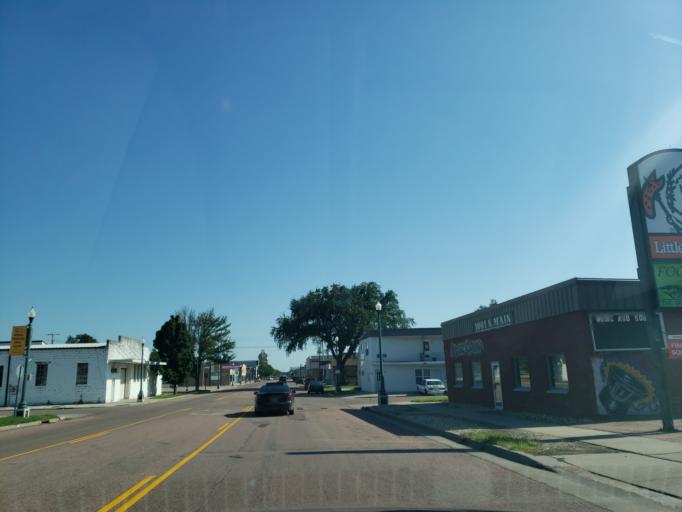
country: US
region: South Dakota
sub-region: Davison County
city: Mitchell
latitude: 43.7191
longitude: -98.0257
